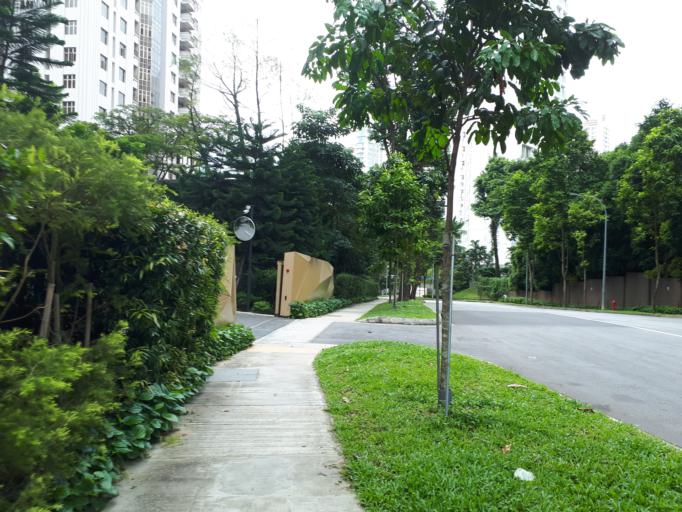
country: SG
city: Singapore
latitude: 1.2984
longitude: 103.8339
